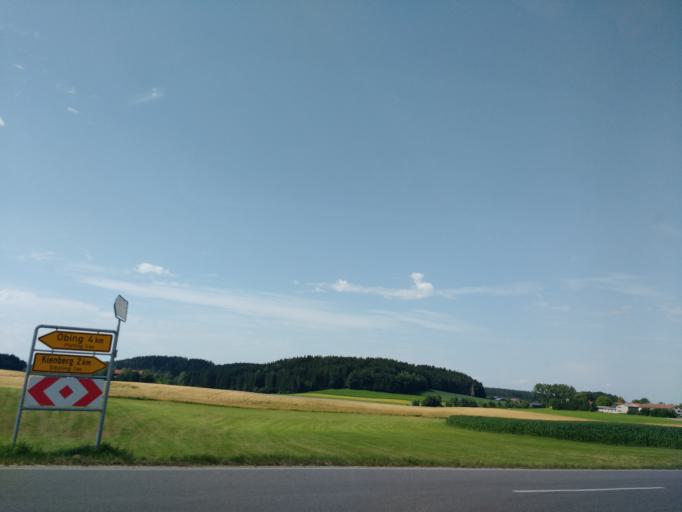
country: DE
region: Bavaria
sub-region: Upper Bavaria
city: Kienberg
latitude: 48.0269
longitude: 12.4372
